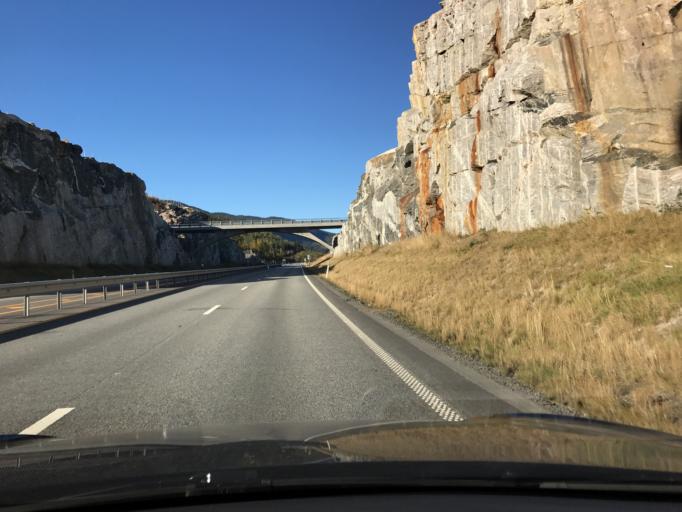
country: NO
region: Buskerud
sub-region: Krodsherad
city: Noresund
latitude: 60.2689
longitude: 9.7840
